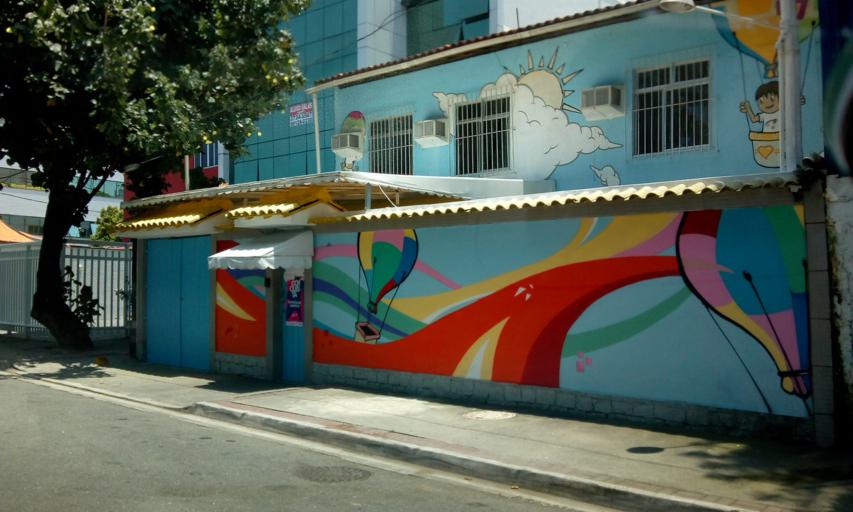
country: BR
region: Rio de Janeiro
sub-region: Nilopolis
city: Nilopolis
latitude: -23.0188
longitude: -43.4603
